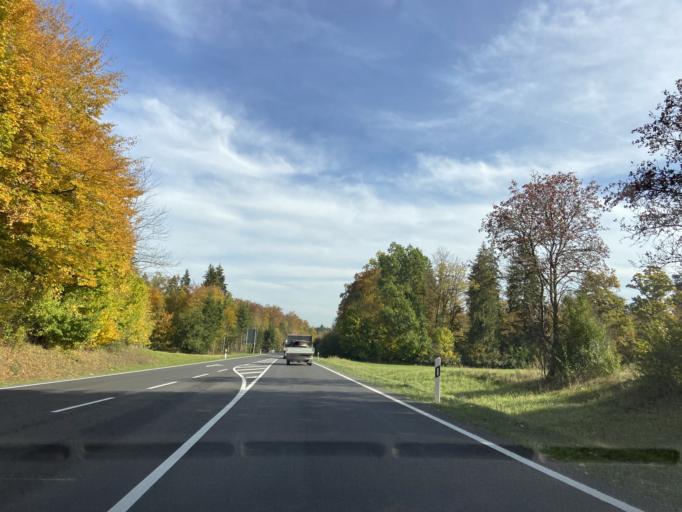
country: DE
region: Baden-Wuerttemberg
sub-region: Tuebingen Region
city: Inzigkofen
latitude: 48.1185
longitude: 9.1771
